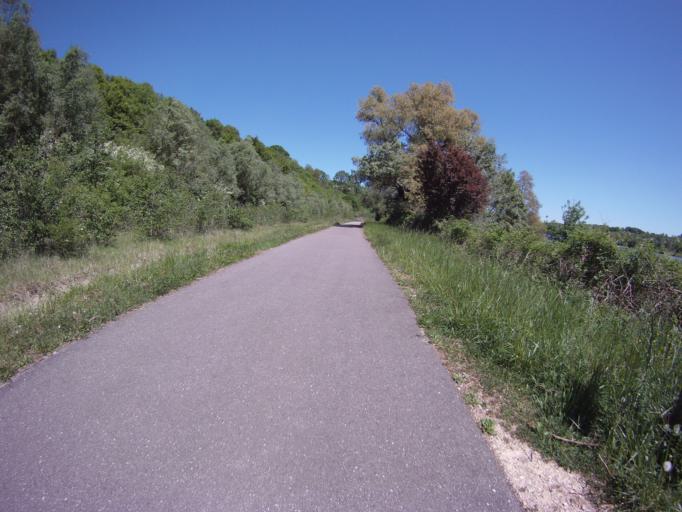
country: FR
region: Lorraine
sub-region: Departement de Meurthe-et-Moselle
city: Villey-Saint-Etienne
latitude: 48.7344
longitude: 5.9837
